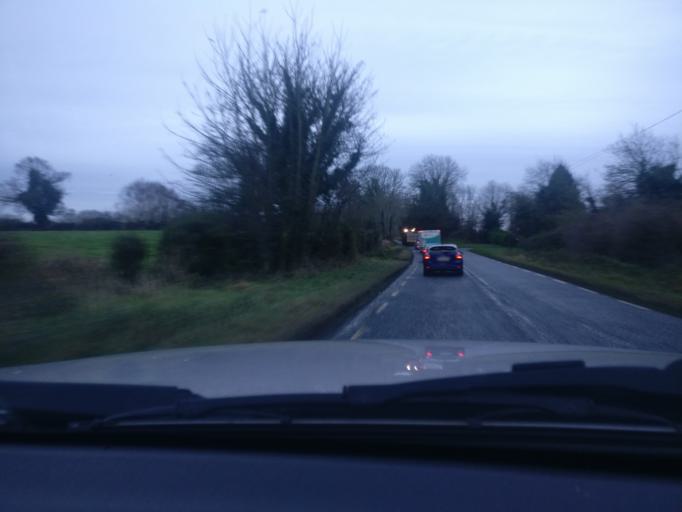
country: IE
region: Leinster
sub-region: An Mhi
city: Kells
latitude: 53.7120
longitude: -6.8183
